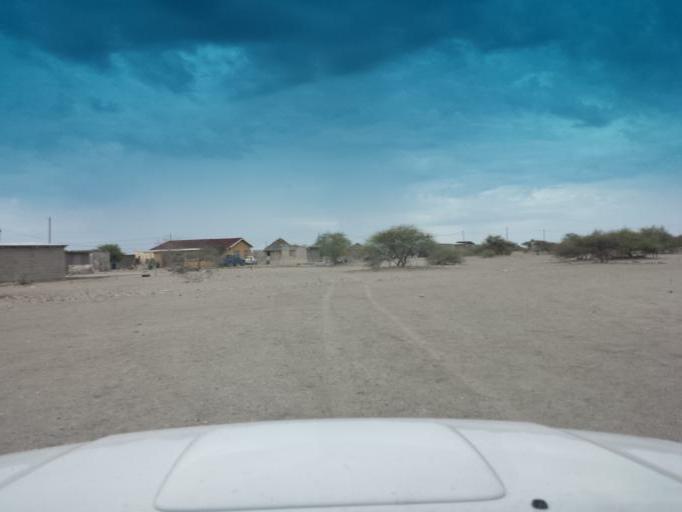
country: BW
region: Central
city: Mopipi
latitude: -21.2011
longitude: 24.8587
